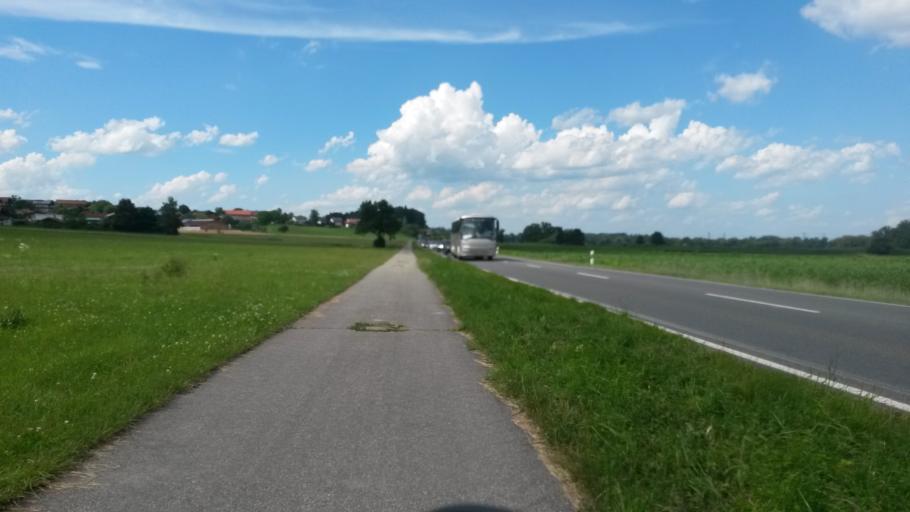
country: DE
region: Bavaria
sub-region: Upper Bavaria
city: Bernau am Chiemsee
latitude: 47.8222
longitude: 12.3613
